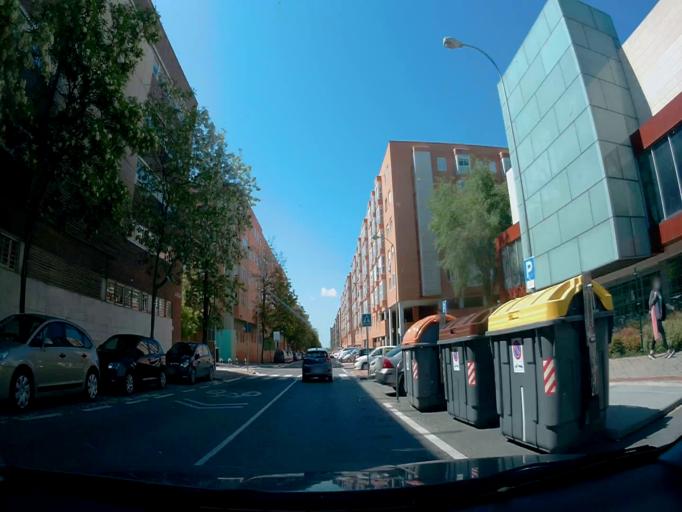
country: ES
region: Madrid
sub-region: Provincia de Madrid
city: Vicalvaro
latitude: 40.4030
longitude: -3.6232
